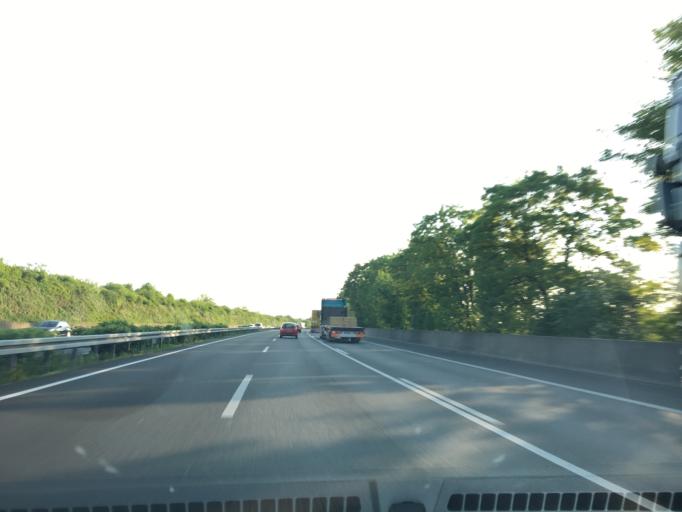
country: DE
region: Lower Saxony
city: Rehren
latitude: 52.2377
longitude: 9.2760
